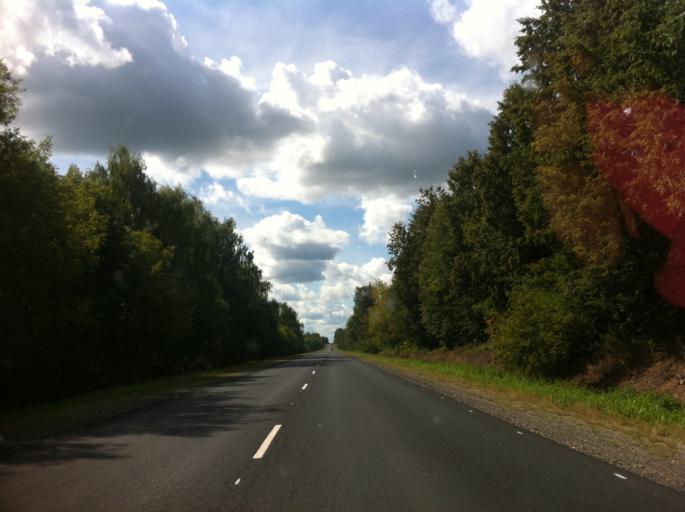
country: RU
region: Pskov
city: Izborsk
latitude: 57.7245
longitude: 27.9495
